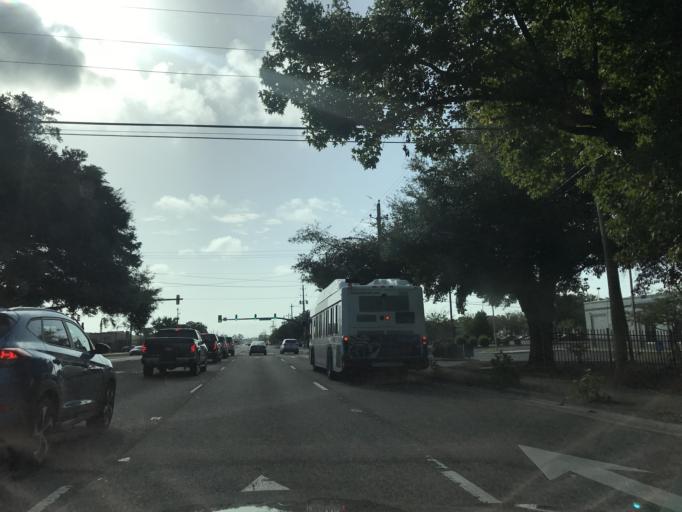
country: US
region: North Carolina
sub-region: New Hanover County
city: Wilmington
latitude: 34.2178
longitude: -77.9080
